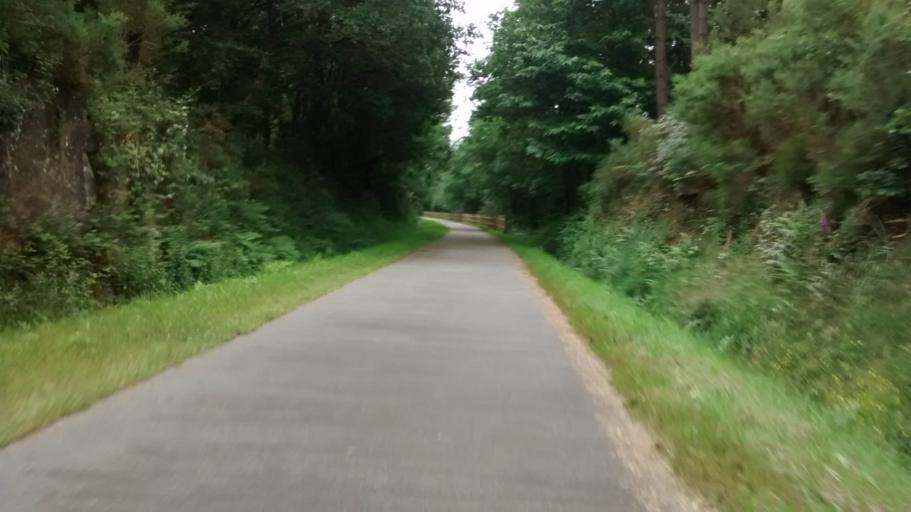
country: FR
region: Brittany
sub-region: Departement du Morbihan
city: Pleucadeuc
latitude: 47.7577
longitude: -2.4006
